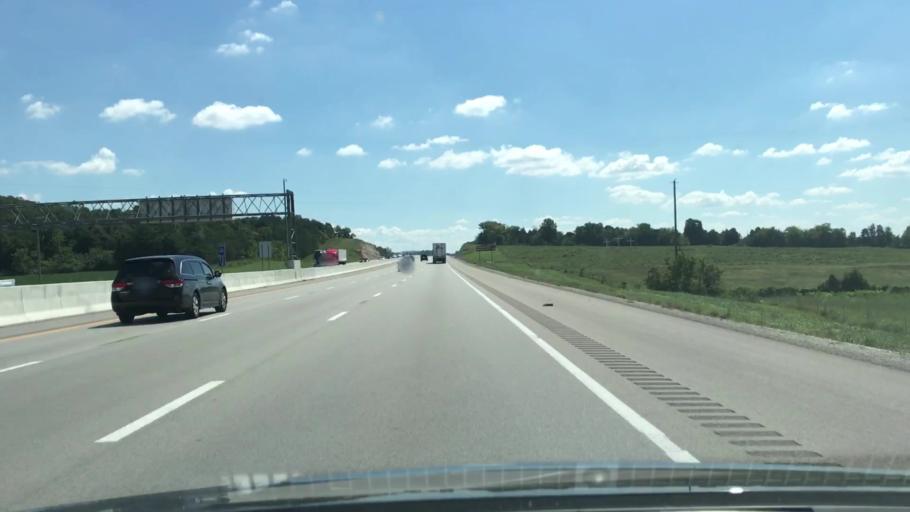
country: US
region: Kentucky
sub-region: Hart County
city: Munfordville
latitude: 37.4282
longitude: -85.8832
